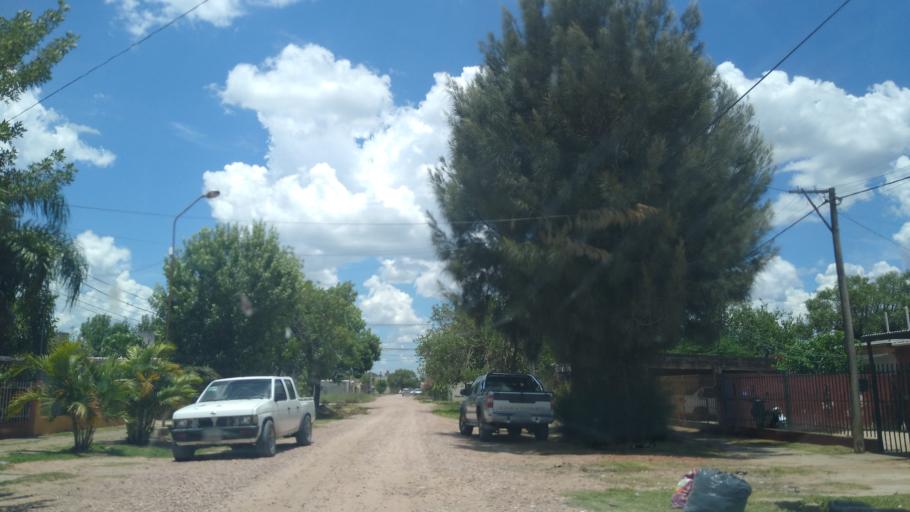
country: AR
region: Chaco
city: Presidencia Roque Saenz Pena
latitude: -26.7722
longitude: -60.4508
